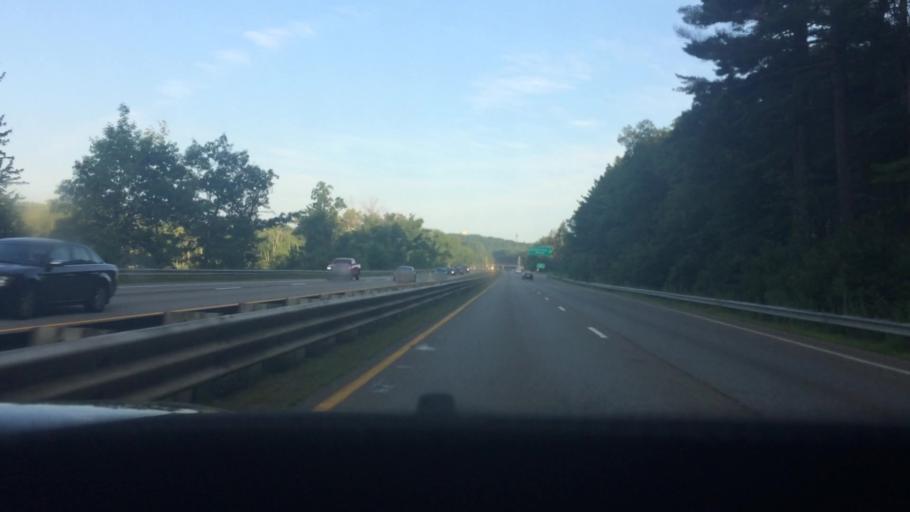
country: US
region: Massachusetts
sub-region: Middlesex County
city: Shirley
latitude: 42.5196
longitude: -71.6258
